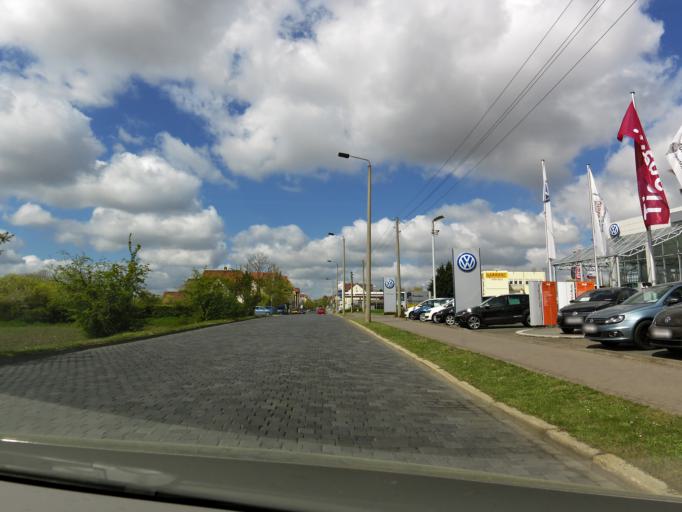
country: DE
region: Thuringia
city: Gotha
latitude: 50.9450
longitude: 10.7349
